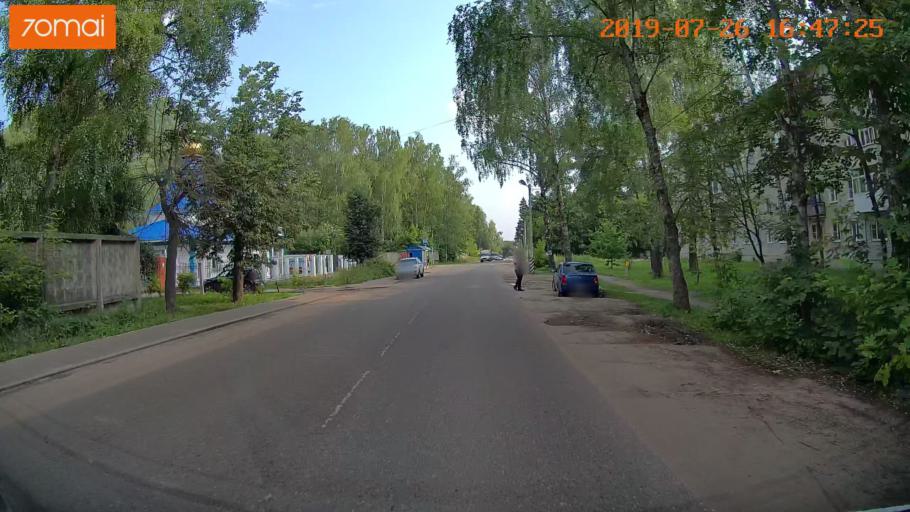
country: RU
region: Ivanovo
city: Bogorodskoye
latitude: 57.0416
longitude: 41.0120
